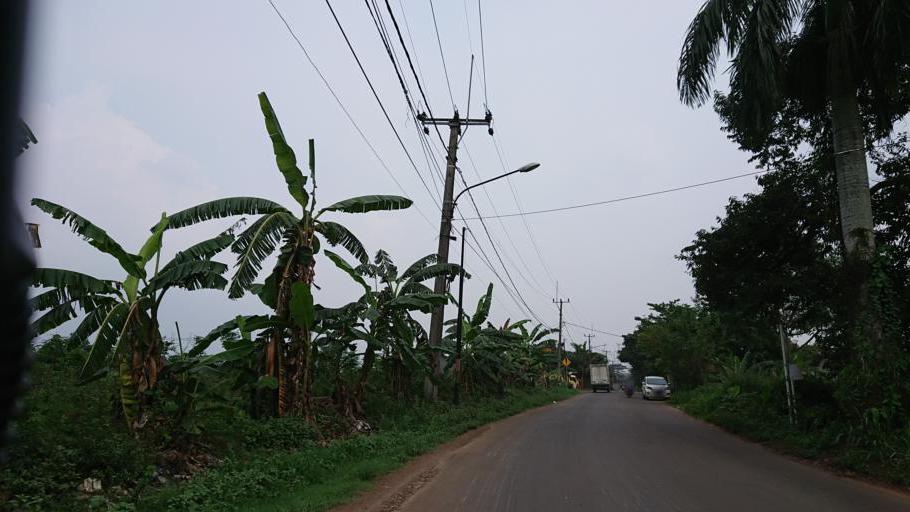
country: ID
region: West Java
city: Parung
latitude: -6.4541
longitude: 106.7042
